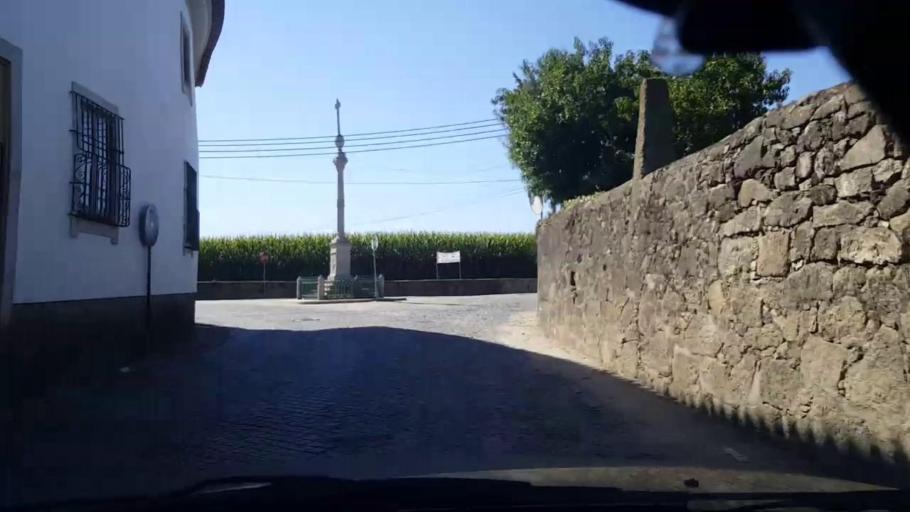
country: PT
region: Porto
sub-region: Vila do Conde
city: Arvore
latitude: 41.3222
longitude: -8.7012
